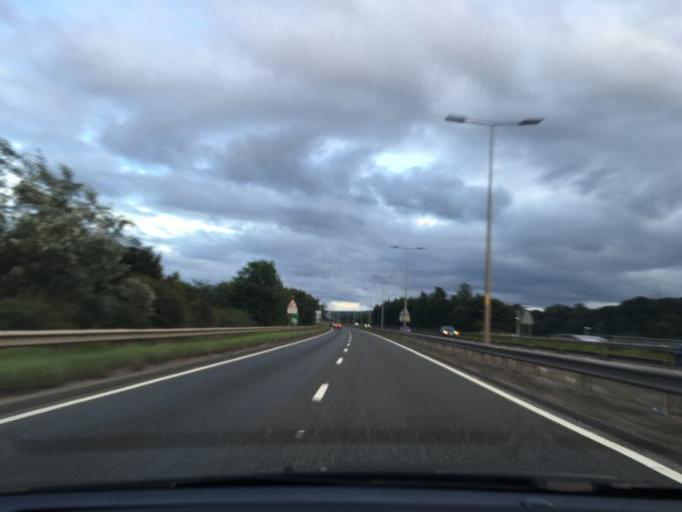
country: GB
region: Scotland
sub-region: Highland
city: Inverness
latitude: 57.4855
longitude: -4.2032
